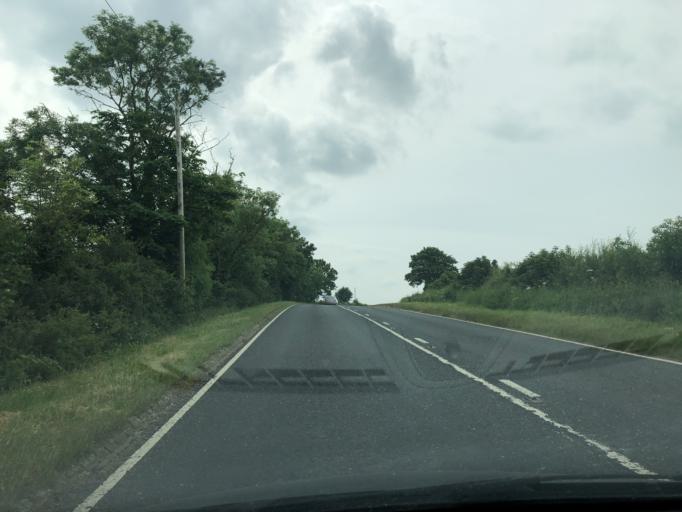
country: GB
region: England
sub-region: North Yorkshire
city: Pickering
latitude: 54.2596
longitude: -0.8397
